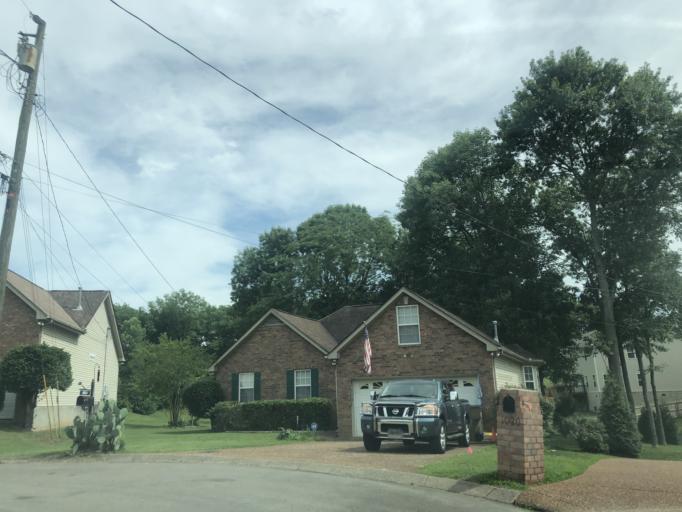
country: US
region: Tennessee
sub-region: Davidson County
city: Nashville
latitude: 36.2132
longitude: -86.8102
